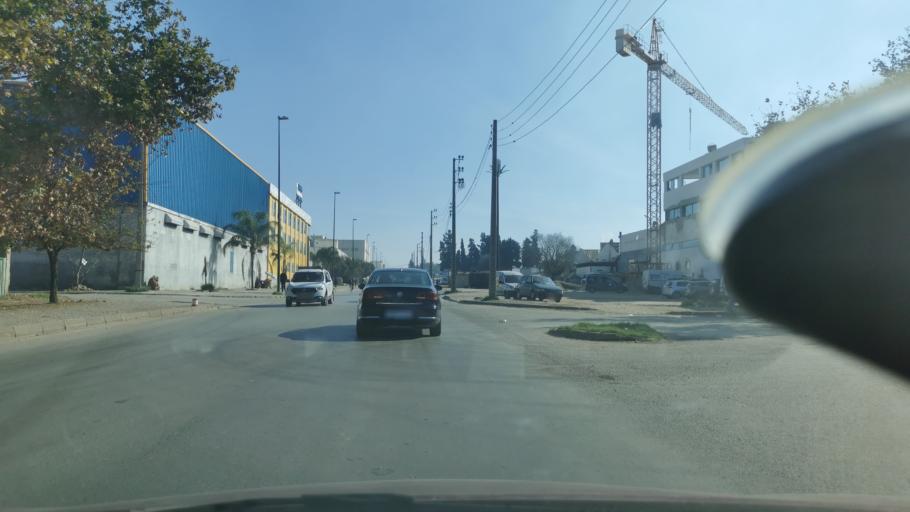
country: MA
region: Fes-Boulemane
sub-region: Fes
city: Fes
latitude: 34.0284
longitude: -4.9806
